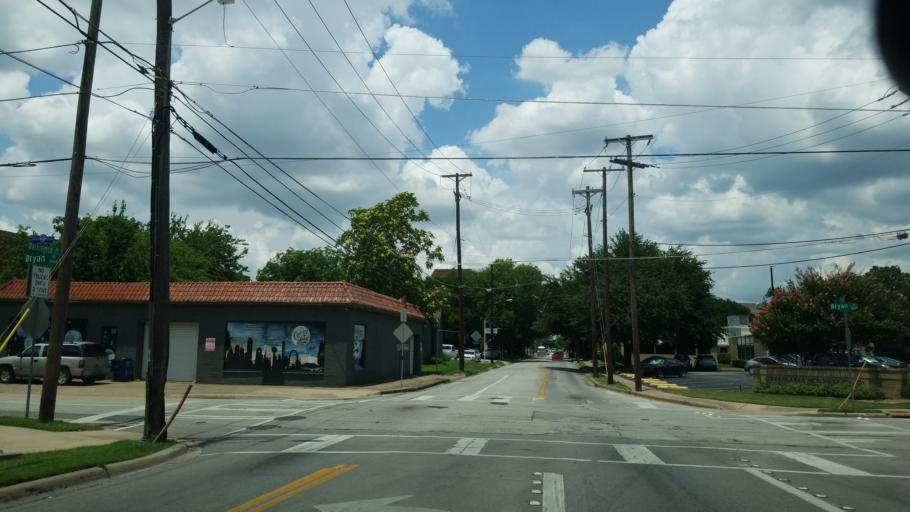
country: US
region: Texas
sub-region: Dallas County
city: Dallas
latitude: 32.7955
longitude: -96.7833
